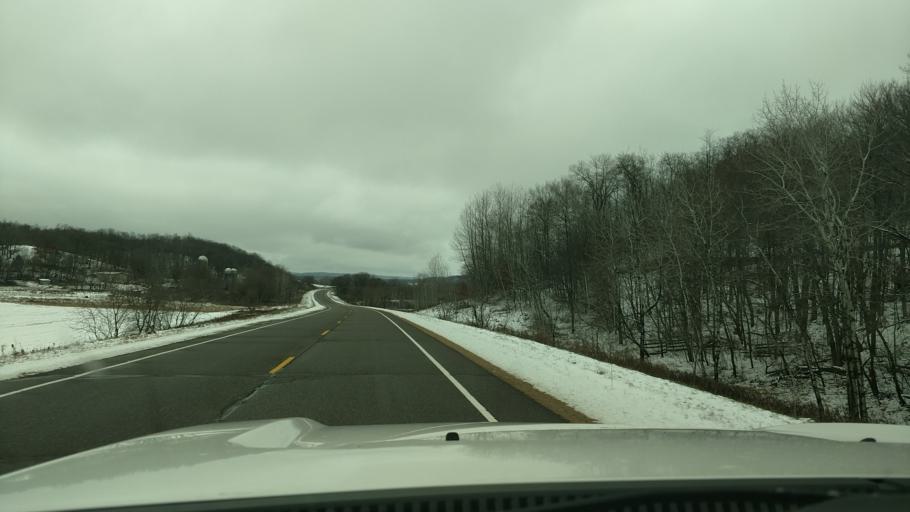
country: US
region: Wisconsin
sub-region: Dunn County
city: Tainter Lake
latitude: 45.1355
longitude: -91.8067
